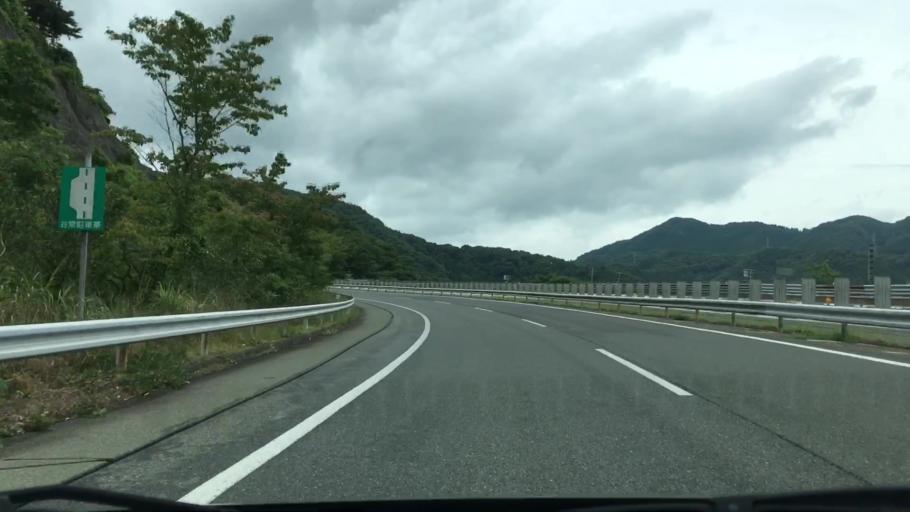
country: JP
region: Hiroshima
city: Shobara
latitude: 34.8989
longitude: 133.2338
